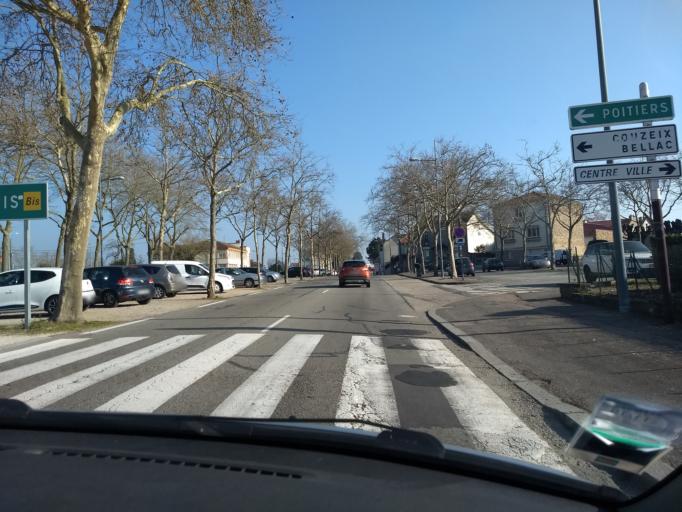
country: FR
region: Limousin
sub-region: Departement de la Haute-Vienne
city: Limoges
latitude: 45.8467
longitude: 1.2438
